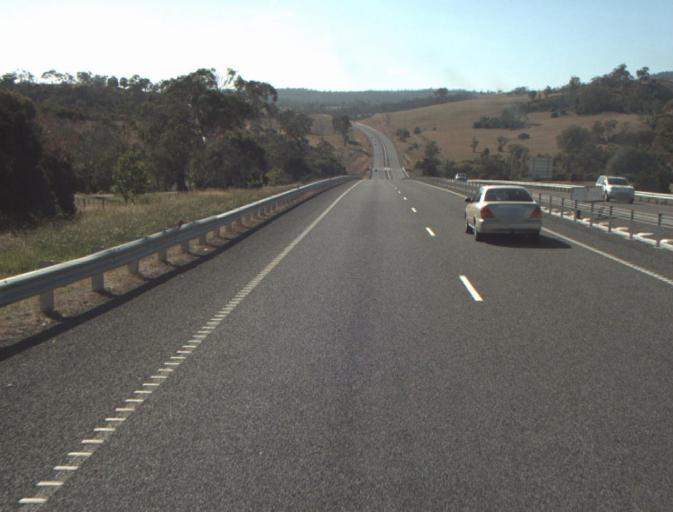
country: AU
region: Tasmania
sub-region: Launceston
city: Mayfield
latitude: -41.3676
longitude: 147.1088
